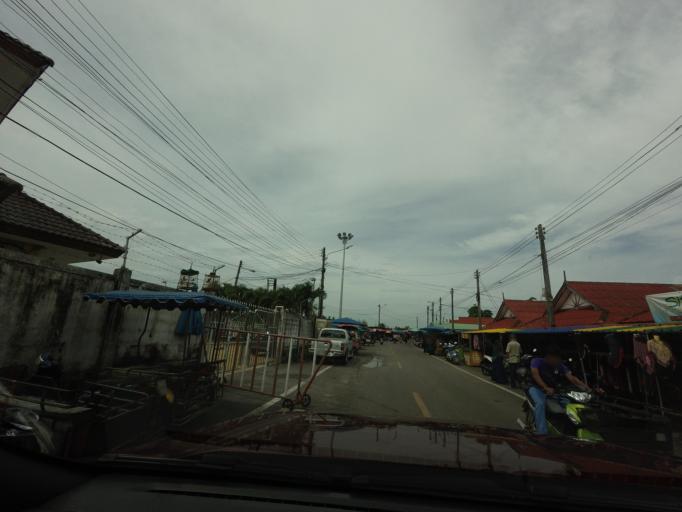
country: TH
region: Narathiwat
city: Tak Bai
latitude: 6.2360
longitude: 102.0898
